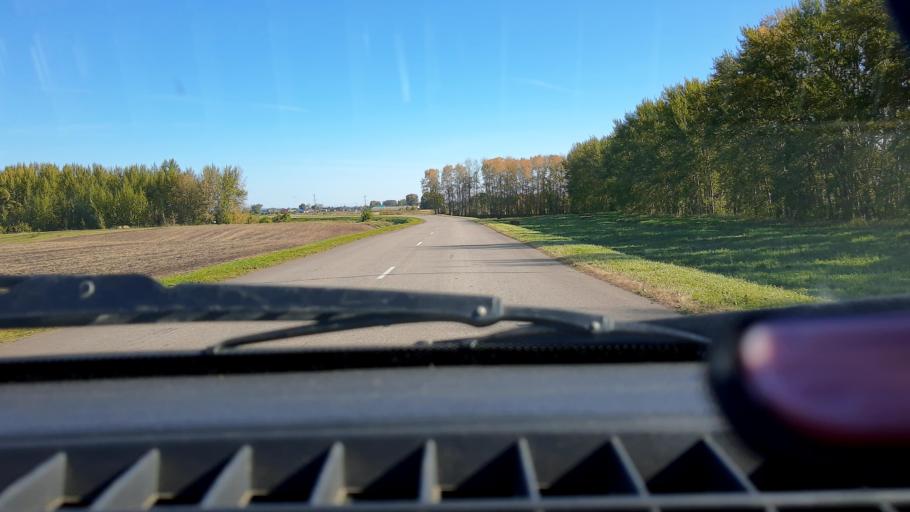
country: RU
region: Bashkortostan
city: Kushnarenkovo
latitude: 55.0829
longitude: 55.4747
